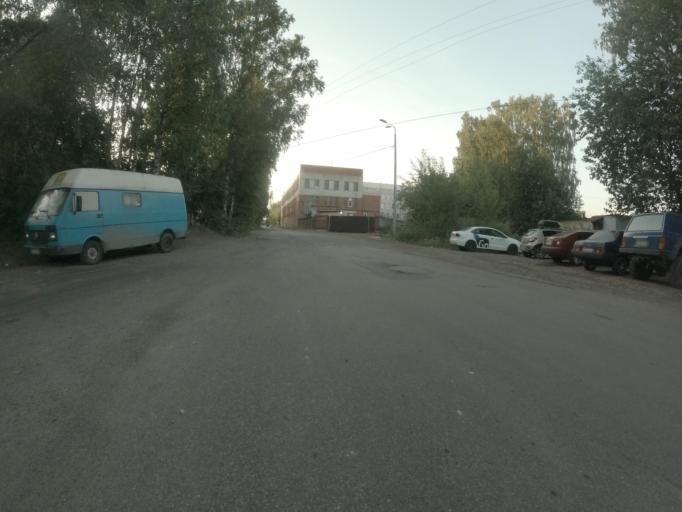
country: RU
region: St.-Petersburg
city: Krasnogvargeisky
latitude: 59.9465
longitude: 30.4414
